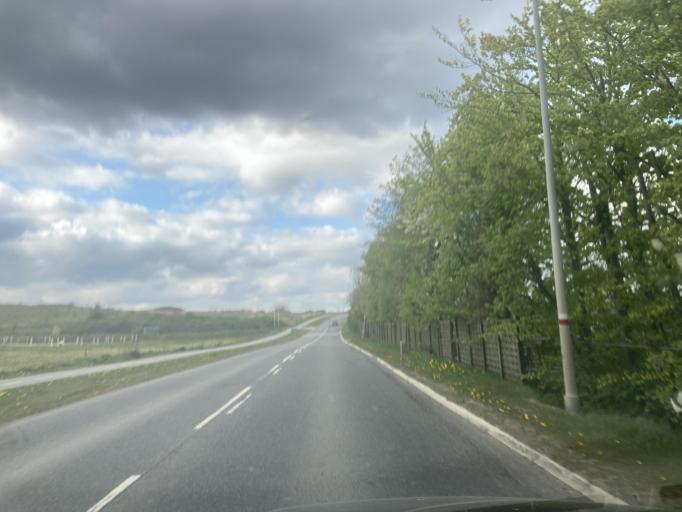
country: DK
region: Zealand
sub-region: Greve Kommune
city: Tune
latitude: 55.6004
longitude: 12.1781
